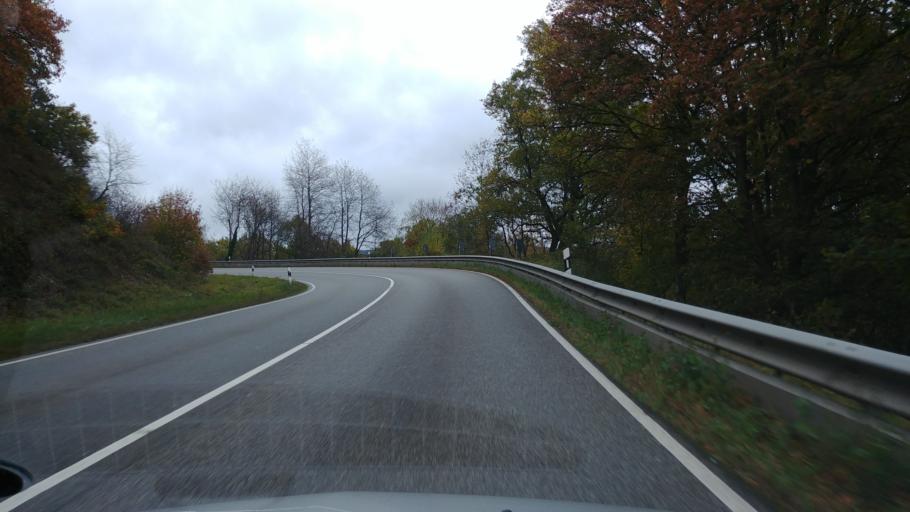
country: DE
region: Rheinland-Pfalz
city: Rorodt
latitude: 49.7833
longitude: 7.0705
